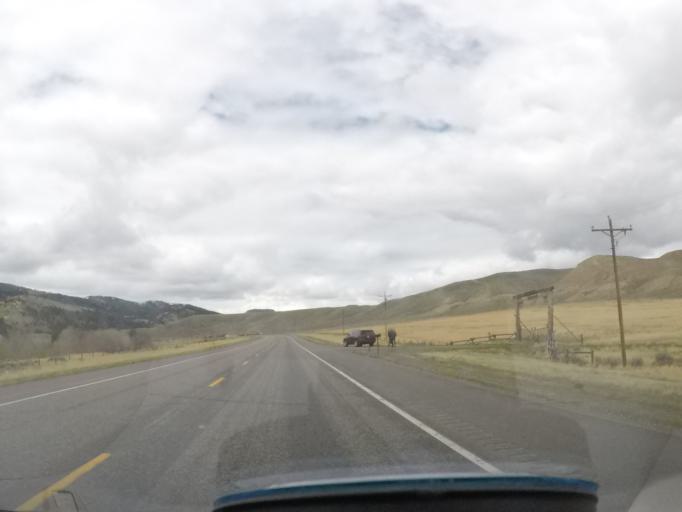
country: US
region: Wyoming
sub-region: Sublette County
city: Pinedale
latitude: 43.5772
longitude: -109.7387
